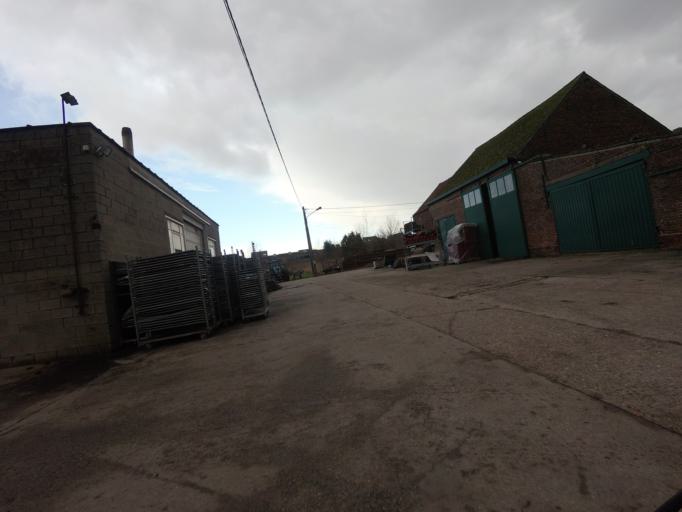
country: BE
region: Flanders
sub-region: Provincie Antwerpen
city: Duffel
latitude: 51.0863
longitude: 4.5132
